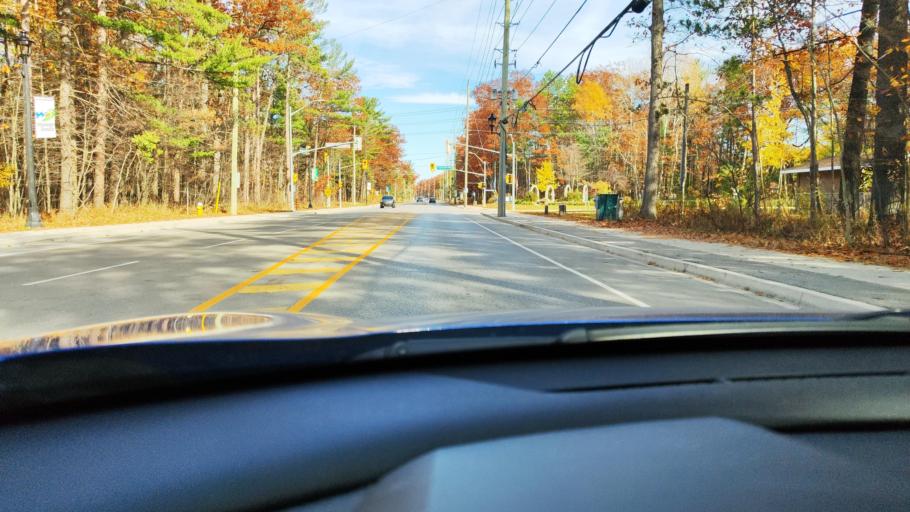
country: CA
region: Ontario
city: Wasaga Beach
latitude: 44.5002
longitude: -80.0375
